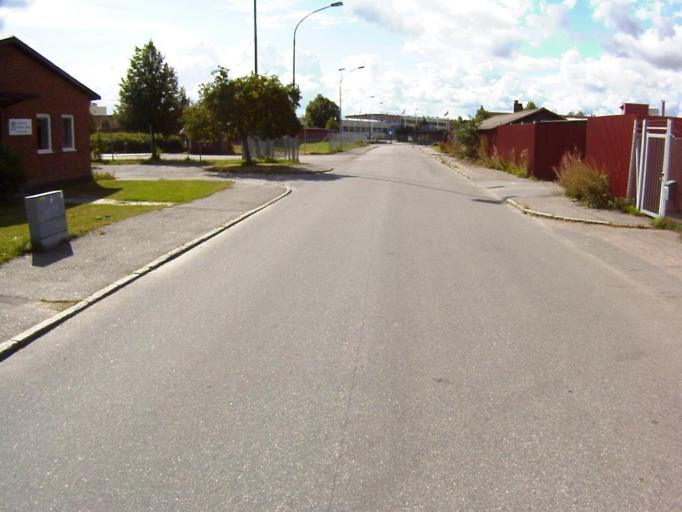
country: SE
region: Soedermanland
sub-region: Eskilstuna Kommun
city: Eskilstuna
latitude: 59.3820
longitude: 16.4919
